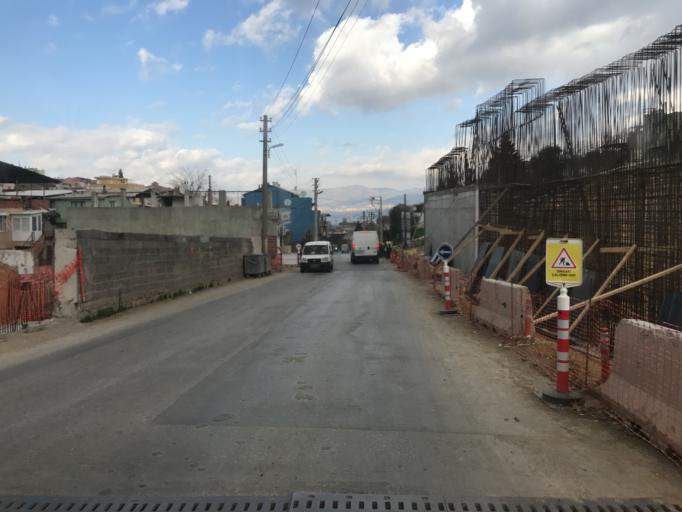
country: TR
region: Izmir
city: Buca
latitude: 38.4051
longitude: 27.1633
